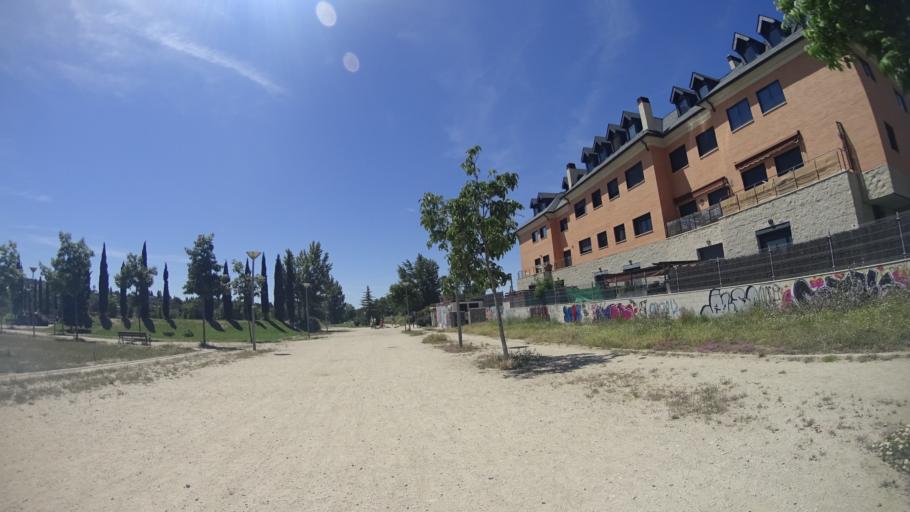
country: ES
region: Madrid
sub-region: Provincia de Madrid
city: Collado-Villalba
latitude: 40.6422
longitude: -4.0068
